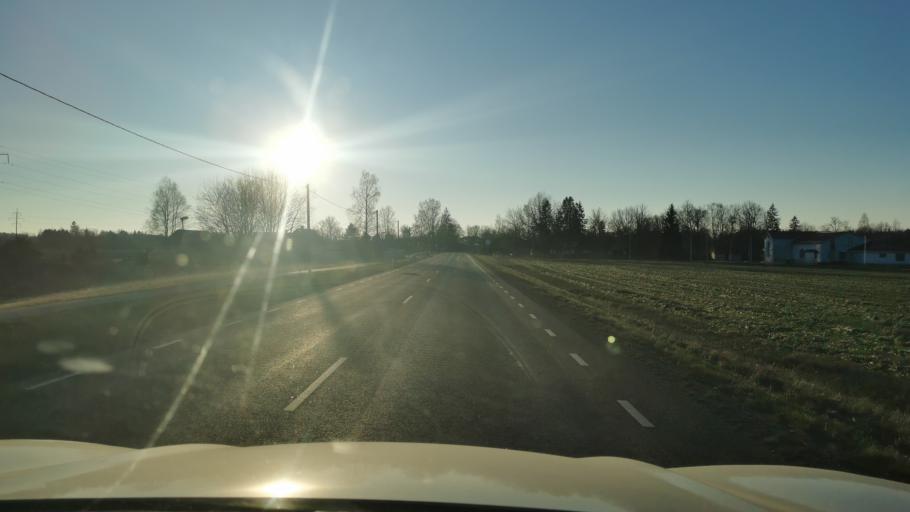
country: EE
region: Ida-Virumaa
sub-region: Kivioli linn
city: Kivioli
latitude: 59.3241
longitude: 27.0113
